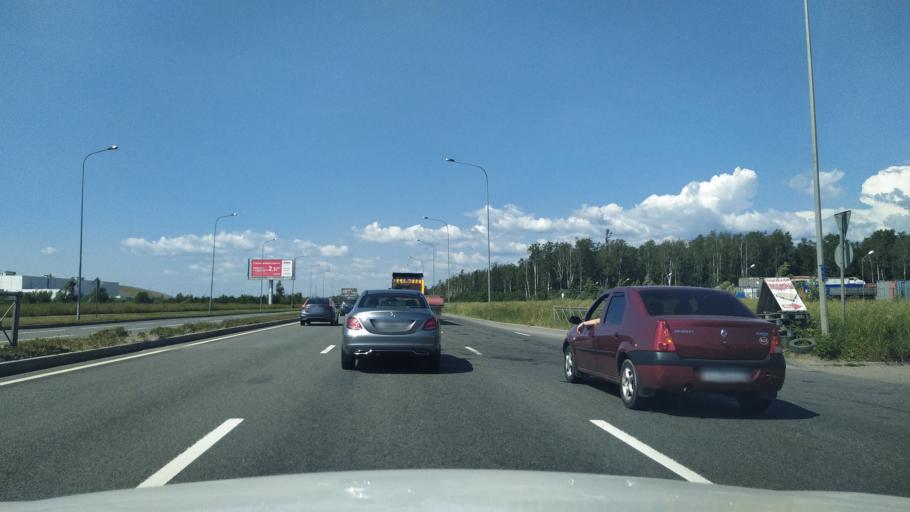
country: RU
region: St.-Petersburg
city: Levashovo
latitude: 60.0651
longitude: 30.1921
